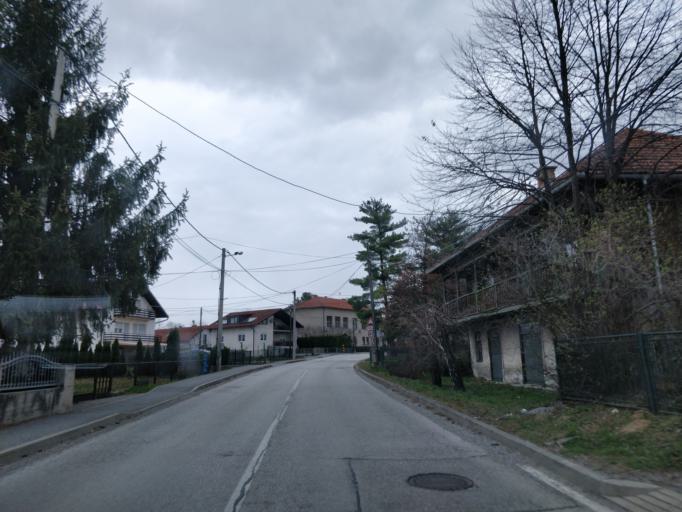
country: HR
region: Zagrebacka
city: Jakovlje
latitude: 45.9183
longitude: 15.8924
